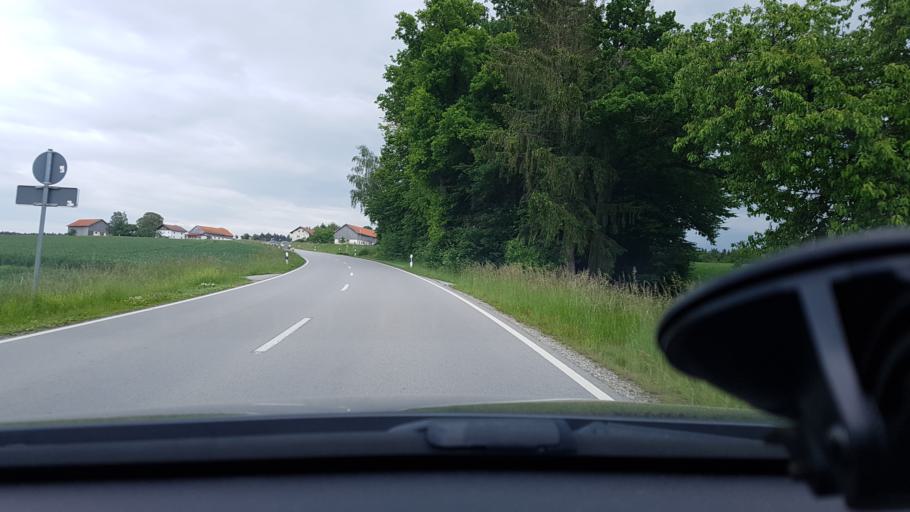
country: DE
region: Bavaria
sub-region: Lower Bavaria
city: Pfarrkirchen
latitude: 48.4140
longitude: 12.9598
